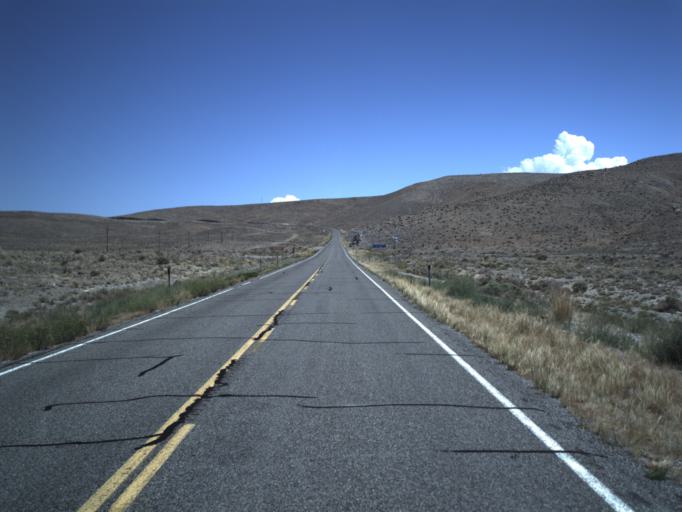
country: US
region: Utah
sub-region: Beaver County
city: Milford
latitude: 39.0238
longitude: -113.3603
